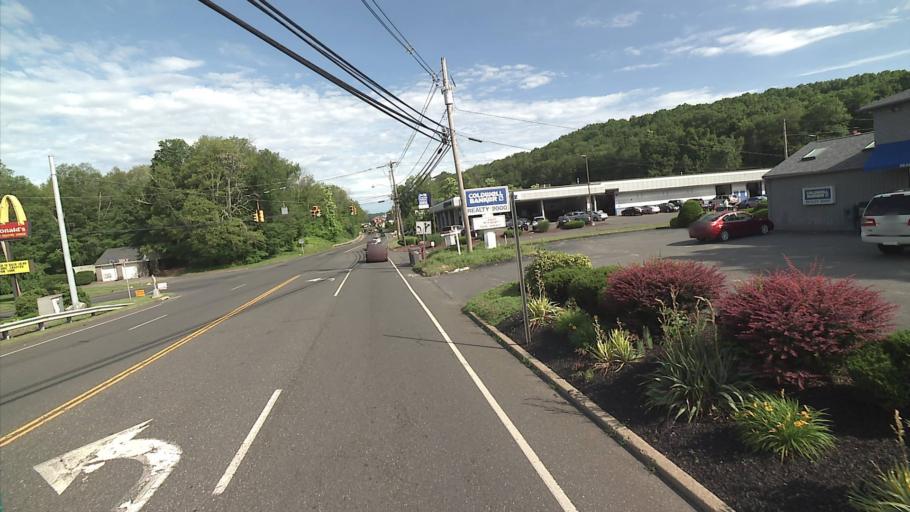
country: US
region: Connecticut
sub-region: New Haven County
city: Naugatuck
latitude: 41.4748
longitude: -73.0430
